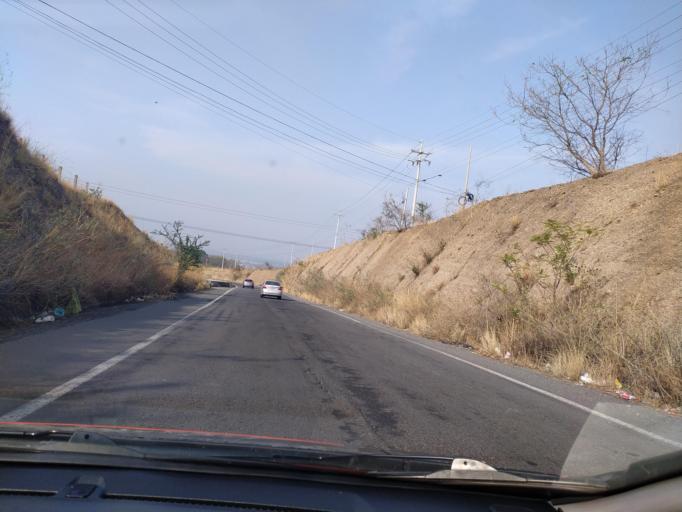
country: MX
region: Jalisco
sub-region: Acatlan de Juarez
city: Villa de los Ninos
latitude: 20.4325
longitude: -103.5810
